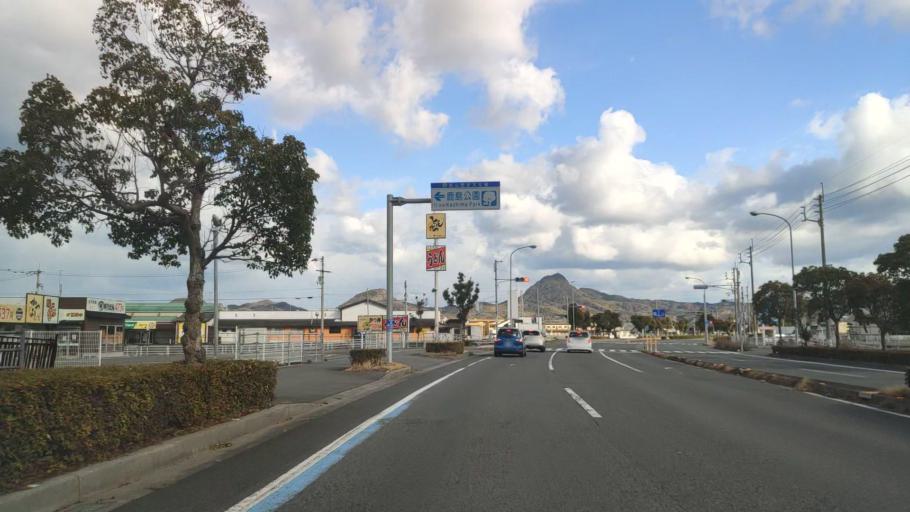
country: JP
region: Ehime
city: Hojo
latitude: 33.9667
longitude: 132.7794
